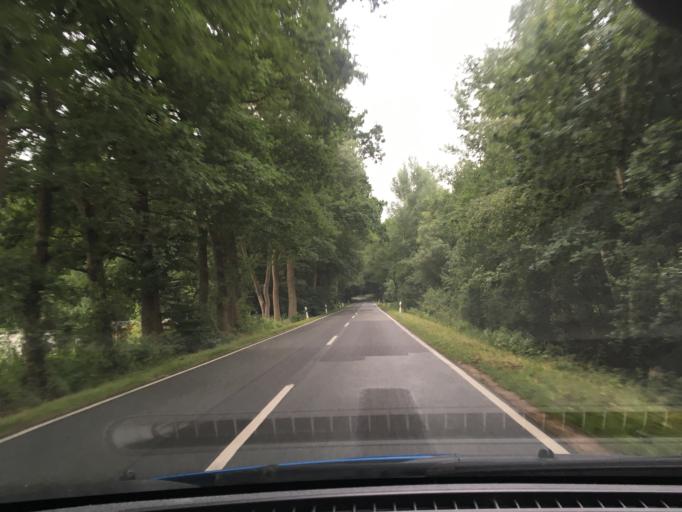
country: DE
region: Lower Saxony
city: Garlstorf
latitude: 53.2247
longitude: 10.0856
